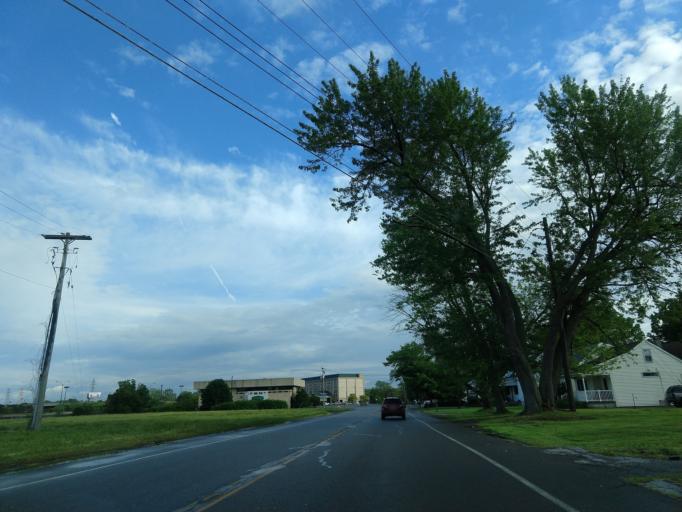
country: US
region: New York
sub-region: Erie County
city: West Seneca
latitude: 42.8330
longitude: -78.7892
